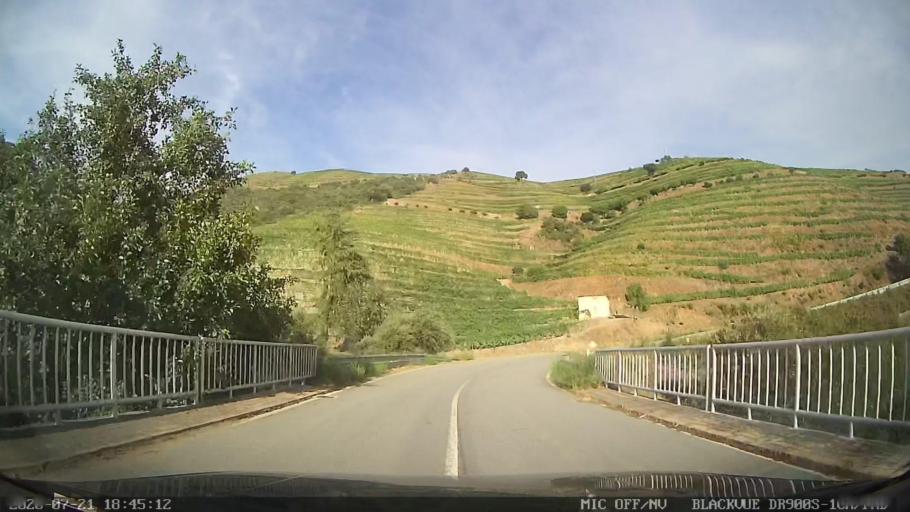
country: PT
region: Viseu
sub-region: Sao Joao da Pesqueira
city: Sao Joao da Pesqueira
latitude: 41.1212
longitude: -7.4486
